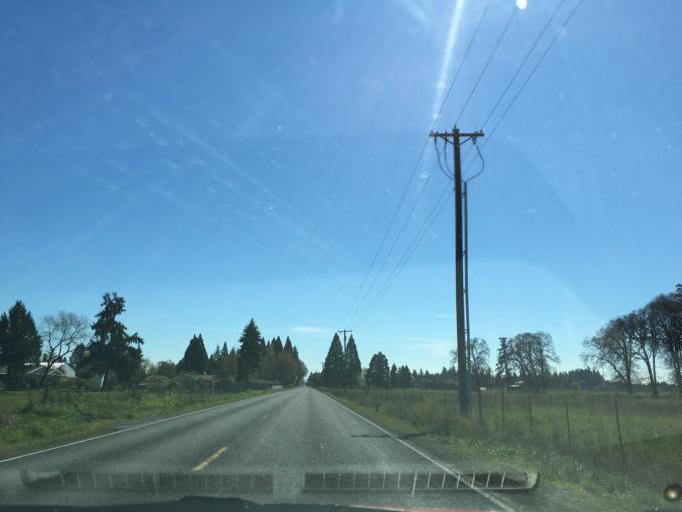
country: US
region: Oregon
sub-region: Clackamas County
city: Canby
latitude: 45.2124
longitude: -122.7228
